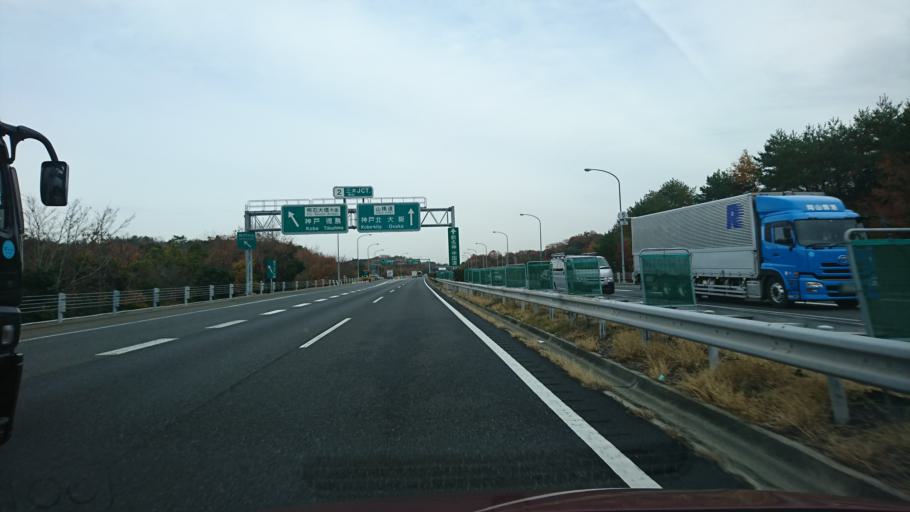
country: JP
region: Hyogo
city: Miki
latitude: 34.8065
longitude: 135.0707
